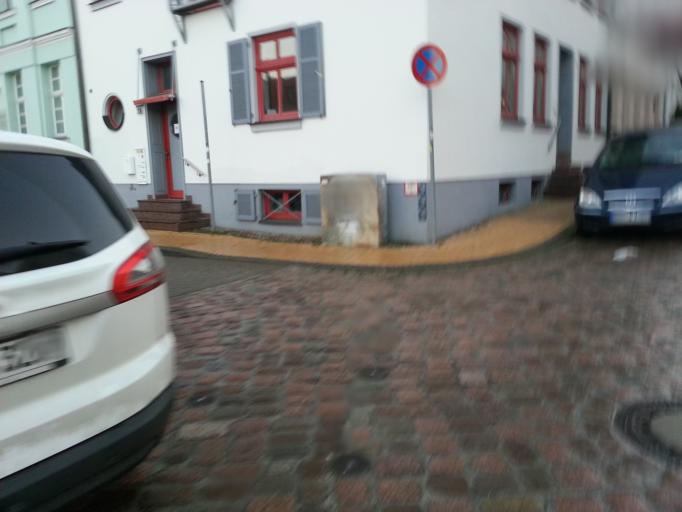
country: DE
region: Mecklenburg-Vorpommern
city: Rostock
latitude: 54.0923
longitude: 12.1382
